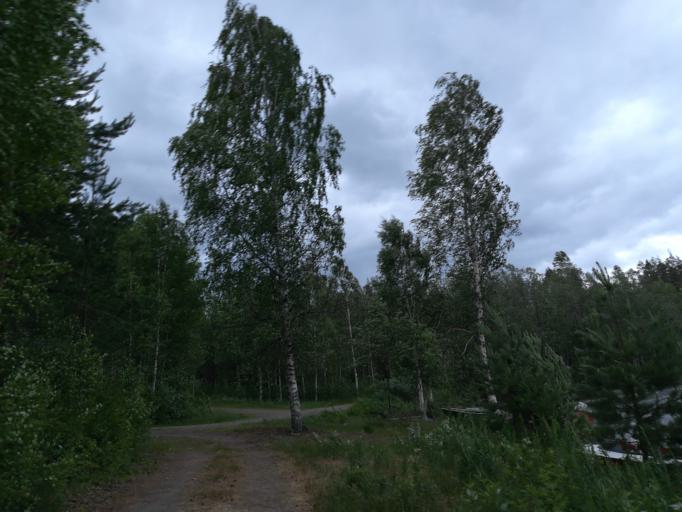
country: FI
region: South Karelia
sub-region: Lappeenranta
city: Savitaipale
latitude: 61.2961
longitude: 27.4820
